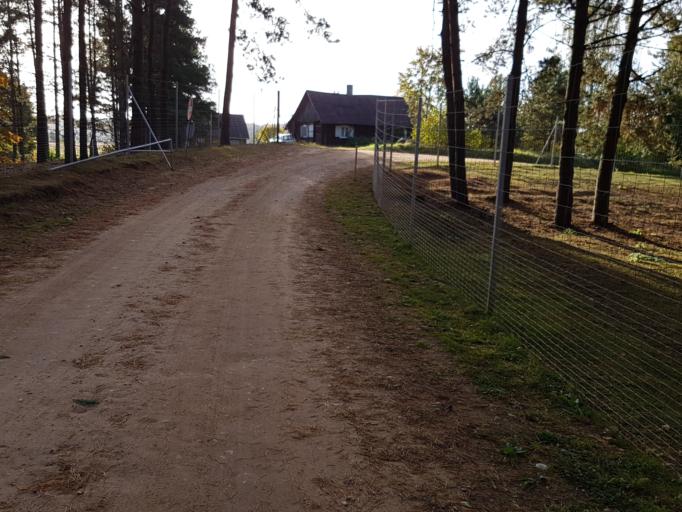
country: LT
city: Moletai
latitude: 55.0388
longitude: 25.4166
